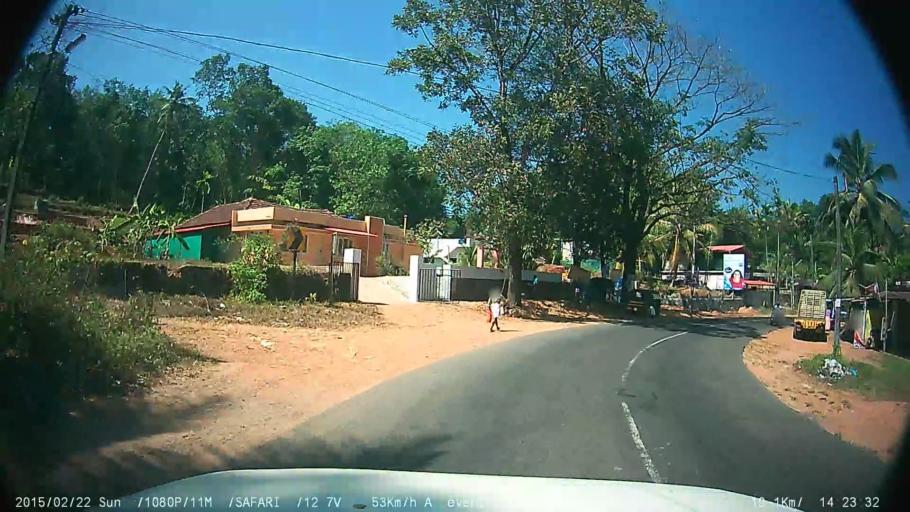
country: IN
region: Kerala
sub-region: Kottayam
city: Lalam
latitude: 9.5672
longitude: 76.7111
